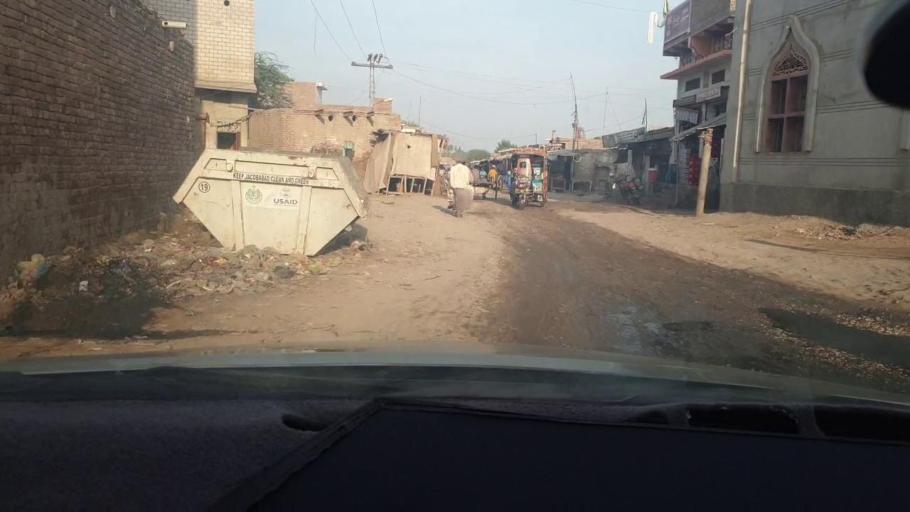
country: PK
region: Sindh
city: Jacobabad
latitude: 28.2838
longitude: 68.4252
